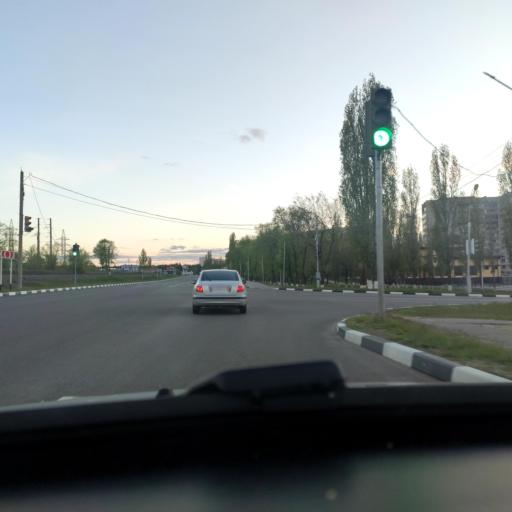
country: RU
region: Voronezj
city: Novovoronezh
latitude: 51.3188
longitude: 39.2238
